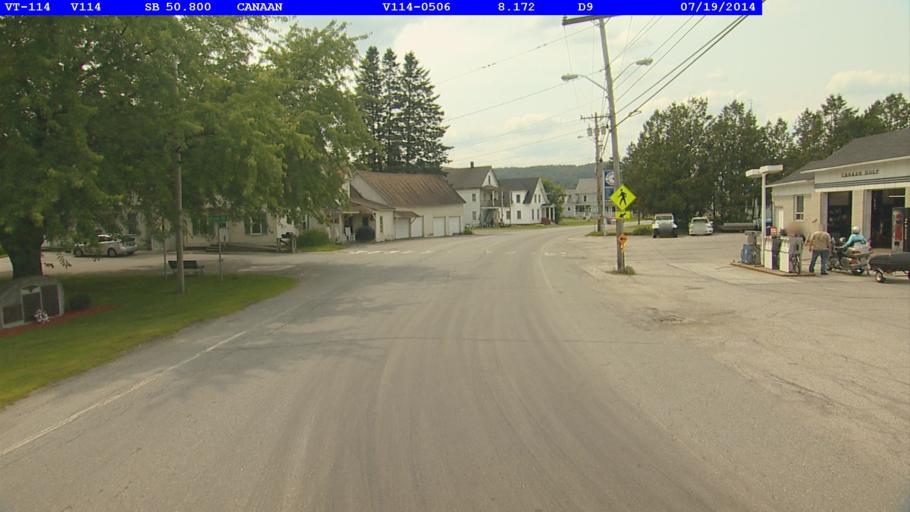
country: US
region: New Hampshire
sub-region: Coos County
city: Colebrook
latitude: 44.9963
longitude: -71.5385
